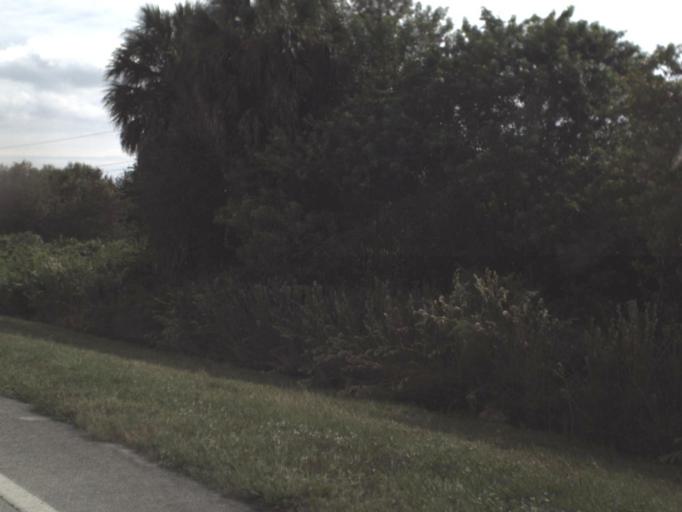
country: US
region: Florida
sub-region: Okeechobee County
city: Taylor Creek
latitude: 27.2157
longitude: -80.7602
